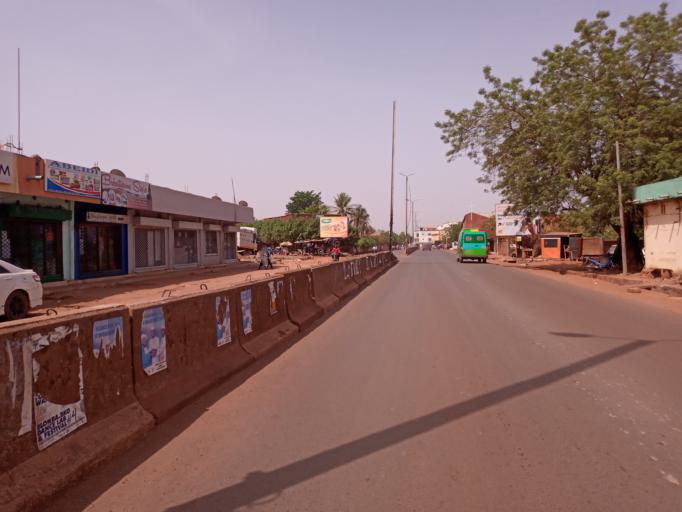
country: ML
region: Bamako
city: Bamako
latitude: 12.6059
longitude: -8.0084
